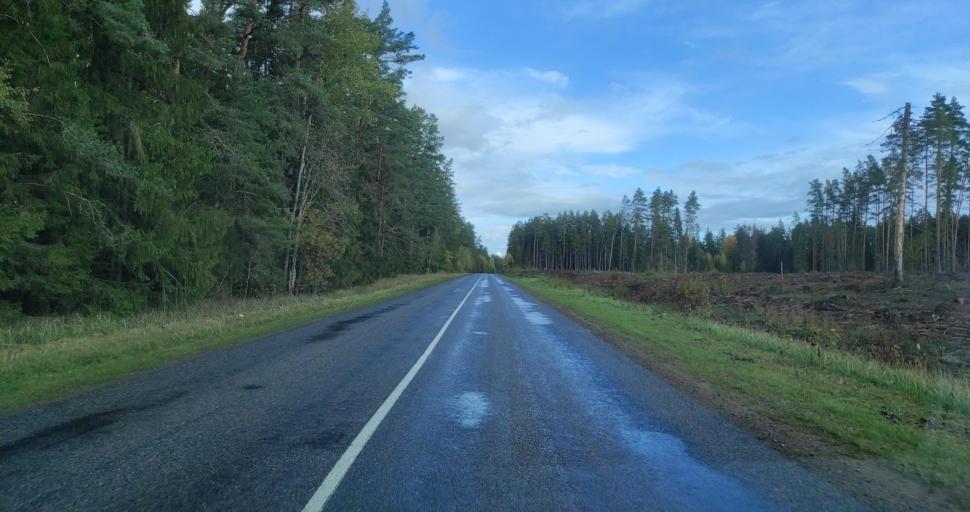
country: LV
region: Skrunda
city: Skrunda
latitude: 56.6369
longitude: 22.0061
